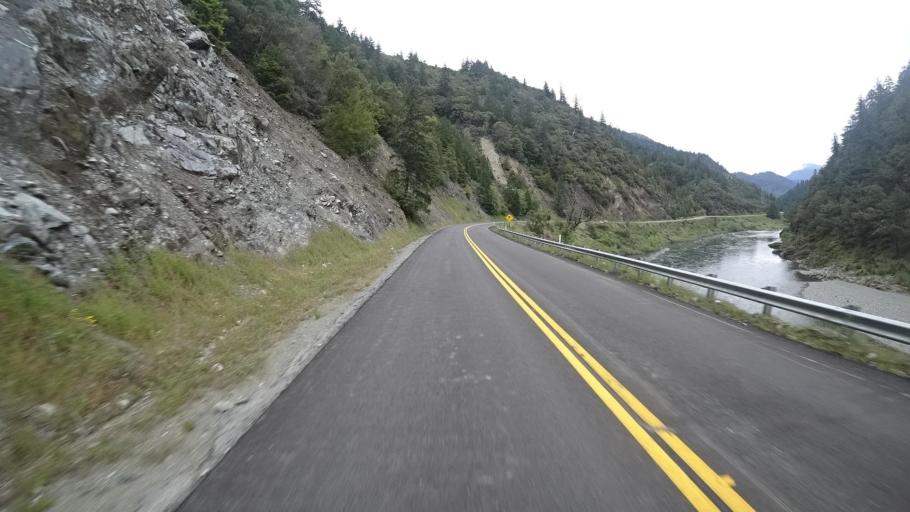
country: US
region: California
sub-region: Humboldt County
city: Willow Creek
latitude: 41.2485
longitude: -123.6490
